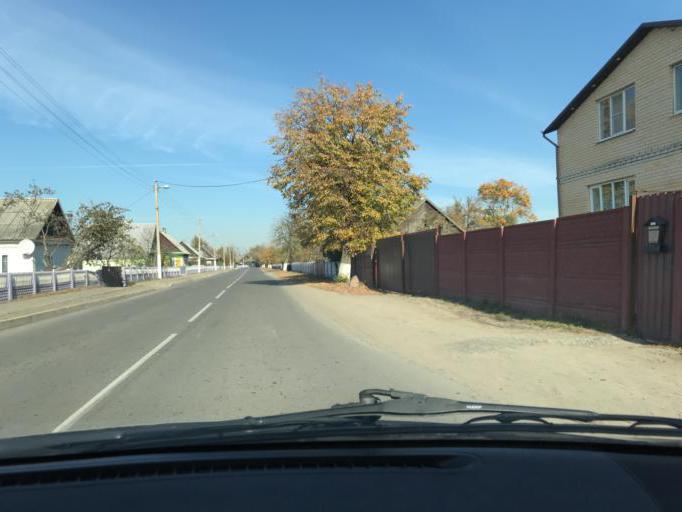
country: BY
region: Brest
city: Mikashevichy
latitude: 52.2252
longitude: 27.4612
